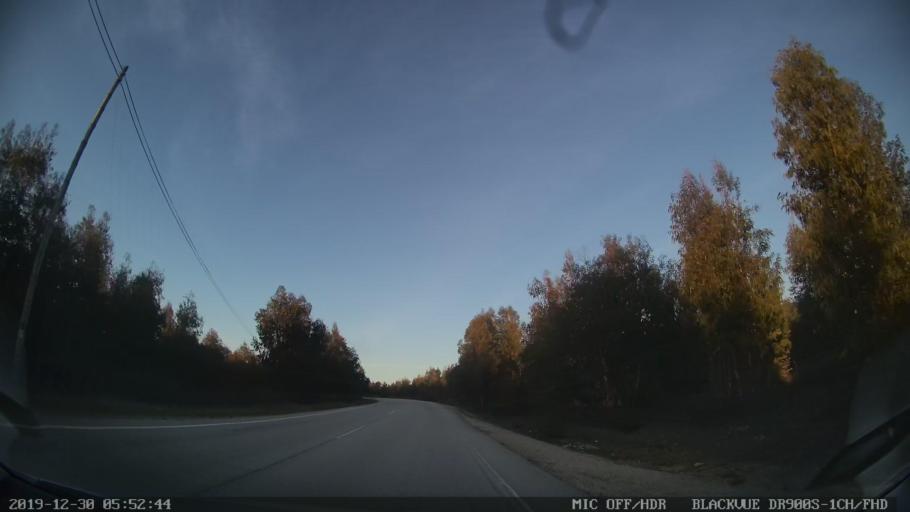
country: PT
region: Castelo Branco
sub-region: Idanha-A-Nova
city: Idanha-a-Nova
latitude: 40.0085
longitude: -7.2489
